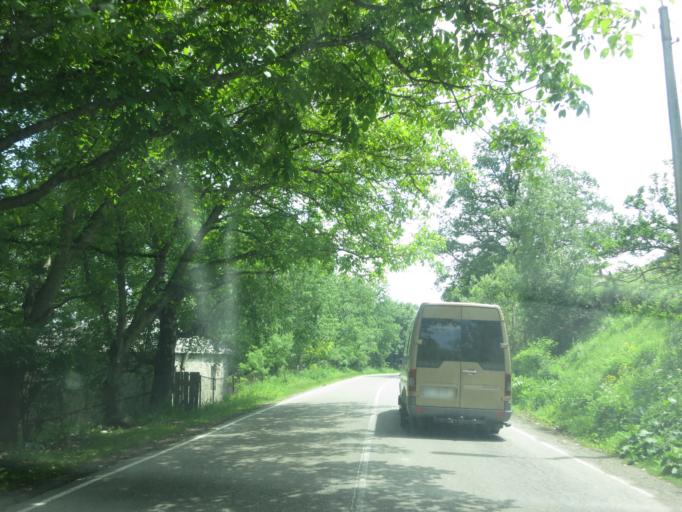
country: GE
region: Kakheti
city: Sagarejo
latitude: 41.8639
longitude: 45.3261
